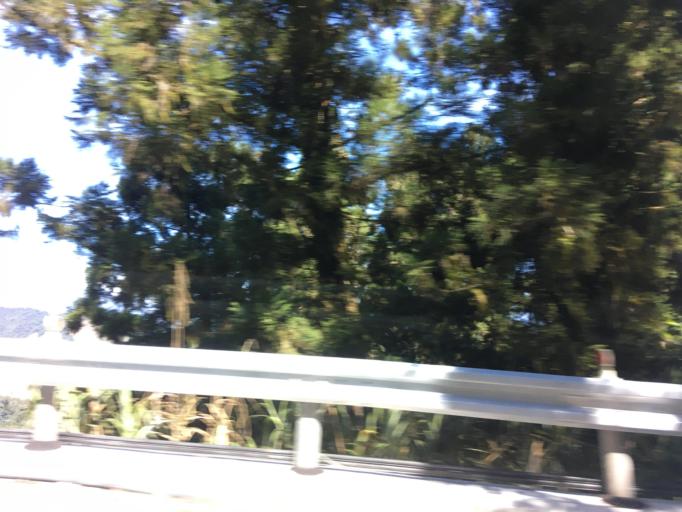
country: TW
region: Taiwan
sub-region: Yilan
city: Yilan
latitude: 24.5342
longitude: 121.5166
